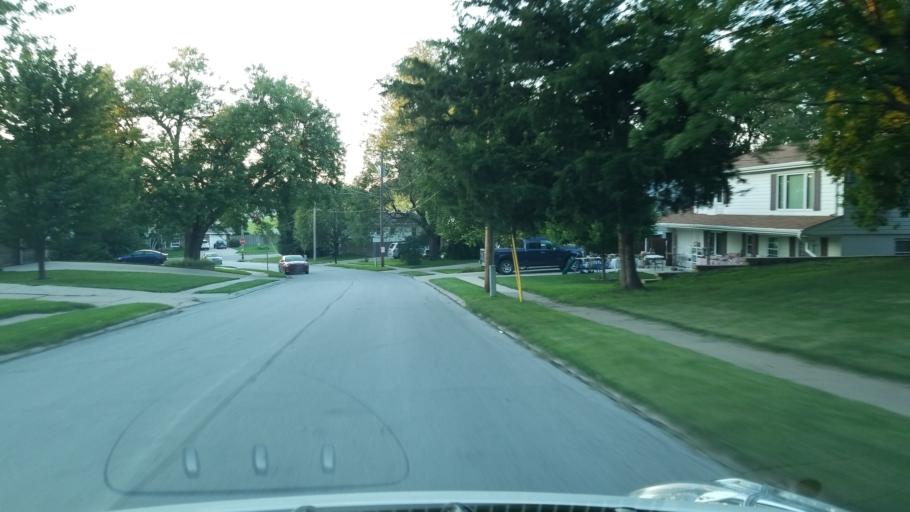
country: US
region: Nebraska
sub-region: Sarpy County
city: Bellevue
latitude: 41.1502
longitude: -95.9122
